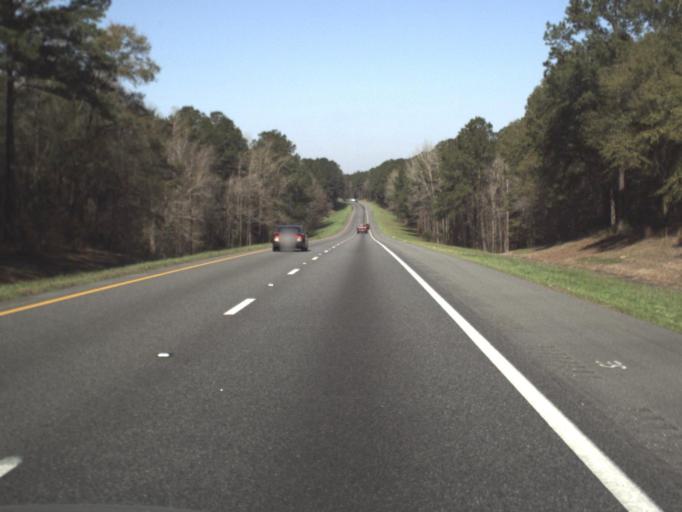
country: US
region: Florida
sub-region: Gadsden County
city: Midway
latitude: 30.5236
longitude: -84.4927
